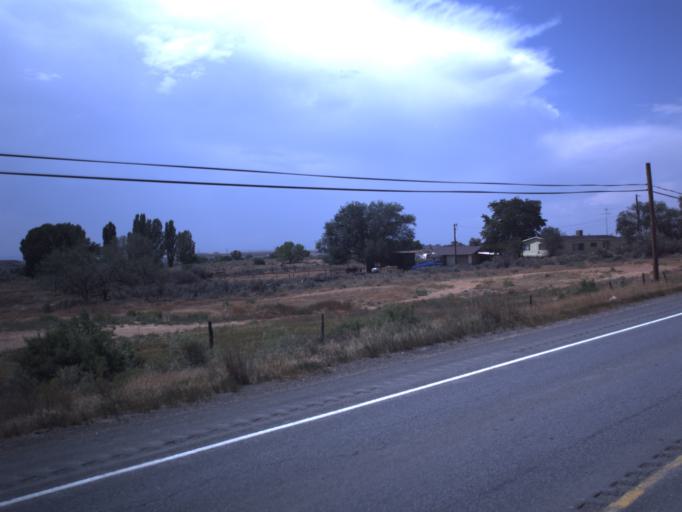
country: US
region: Utah
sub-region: Duchesne County
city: Roosevelt
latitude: 40.3020
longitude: -109.8295
